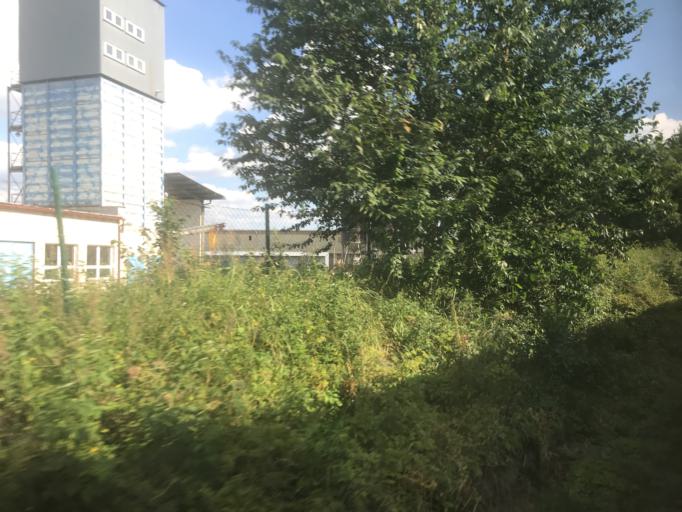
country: CZ
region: Jihocesky
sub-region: Okres Cesky Krumlov
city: Kaplice
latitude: 48.7207
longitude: 14.4463
